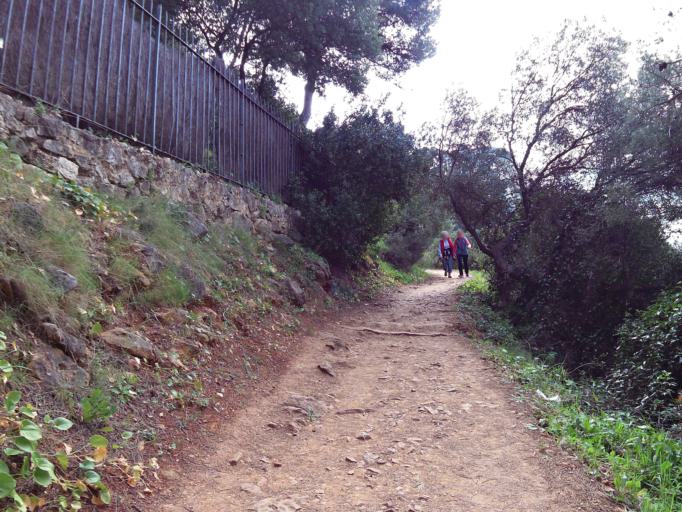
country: FR
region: Provence-Alpes-Cote d'Azur
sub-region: Departement des Alpes-Maritimes
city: Saint-Jean-Cap-Ferrat
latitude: 43.6827
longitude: 7.3247
